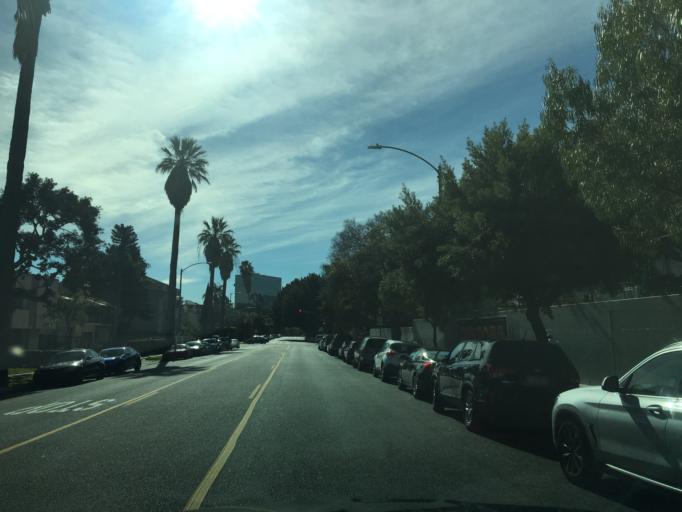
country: US
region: California
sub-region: Los Angeles County
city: Silver Lake
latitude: 34.0700
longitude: -118.2858
